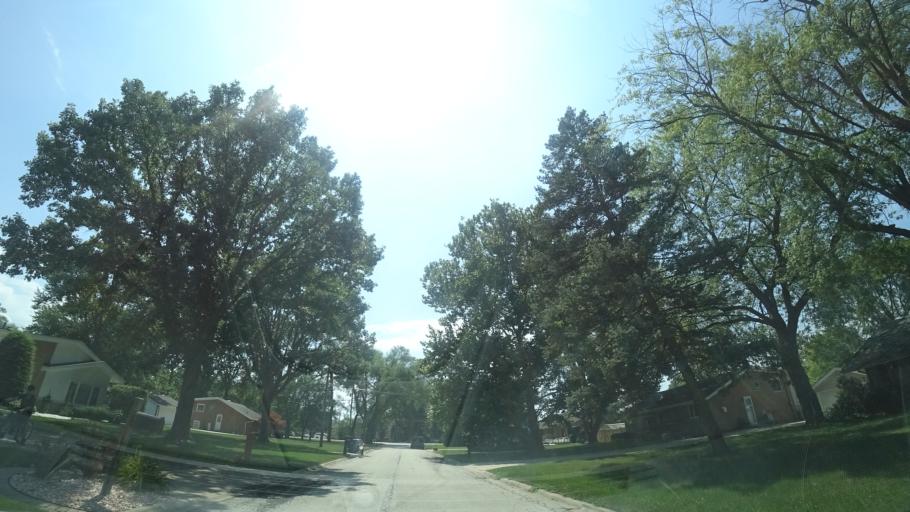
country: US
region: Illinois
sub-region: Cook County
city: Crestwood
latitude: 41.6623
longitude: -87.7606
